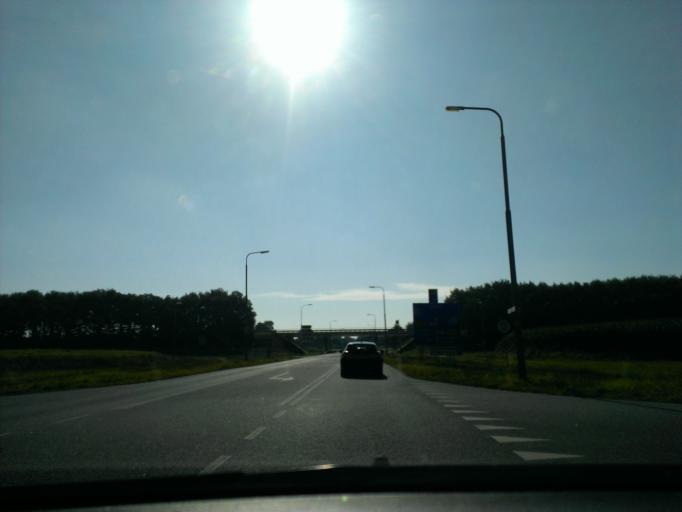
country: NL
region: Drenthe
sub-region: Gemeente Coevorden
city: Dalen
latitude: 52.7090
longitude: 6.7498
